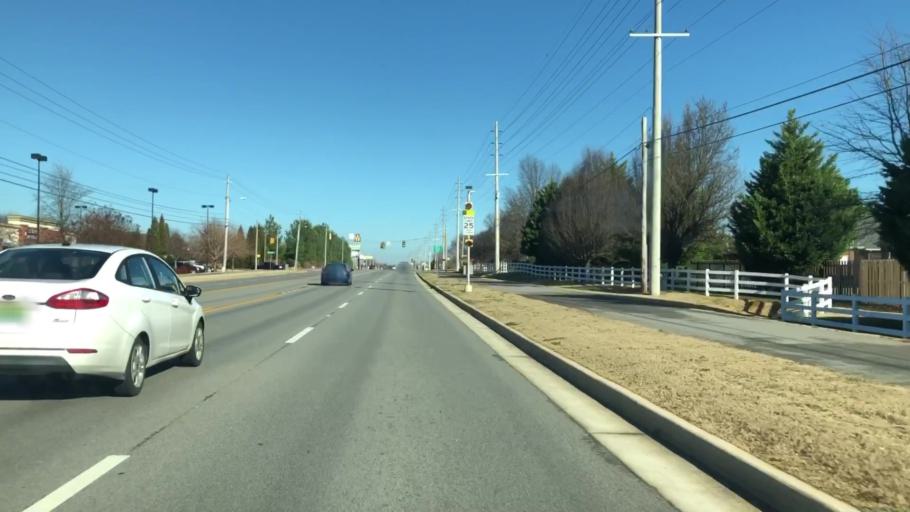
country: US
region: Alabama
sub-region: Madison County
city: Madison
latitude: 34.7312
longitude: -86.7863
